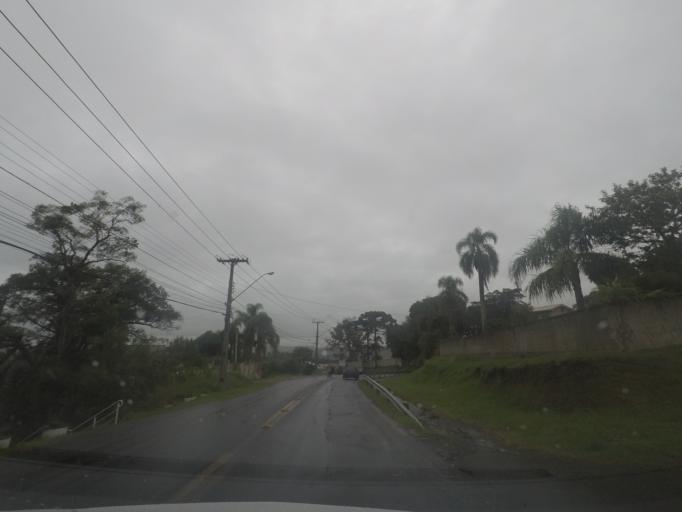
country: BR
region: Parana
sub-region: Quatro Barras
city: Quatro Barras
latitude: -25.3756
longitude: -49.1129
